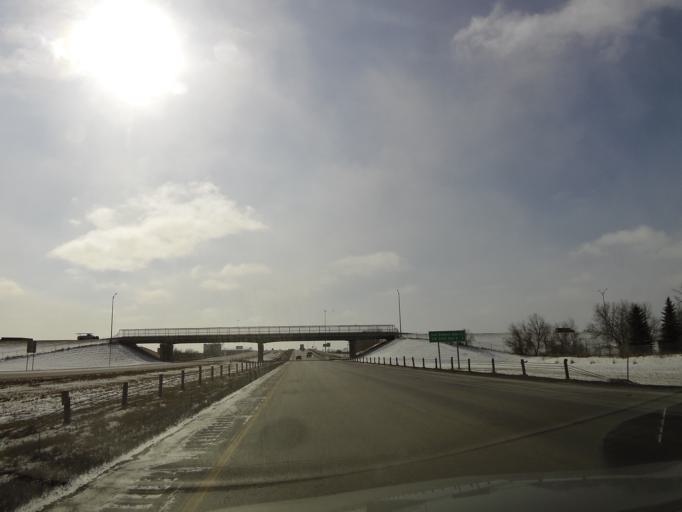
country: US
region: North Dakota
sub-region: Grand Forks County
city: Grand Forks
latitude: 47.9236
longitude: -97.0937
